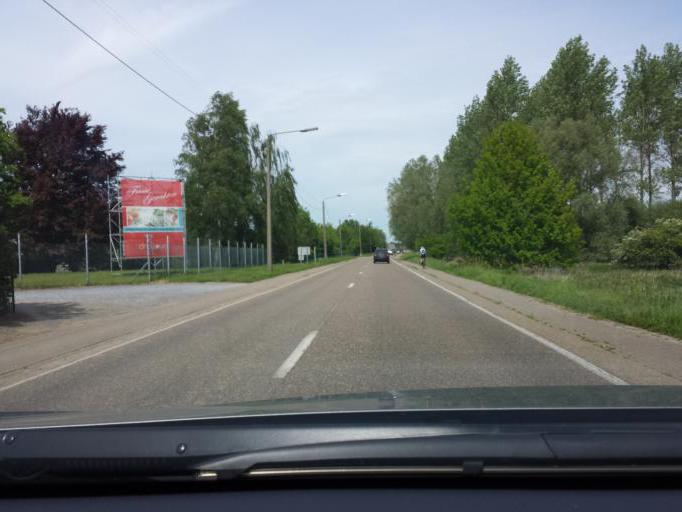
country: BE
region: Flanders
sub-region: Provincie Limburg
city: Halen
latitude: 50.9560
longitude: 5.1165
